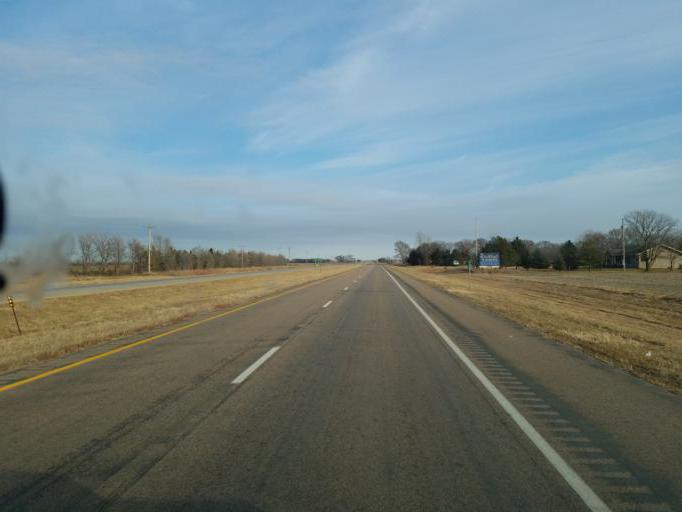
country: US
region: South Dakota
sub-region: Union County
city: Dakota Dunes
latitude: 42.4483
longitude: -96.5335
